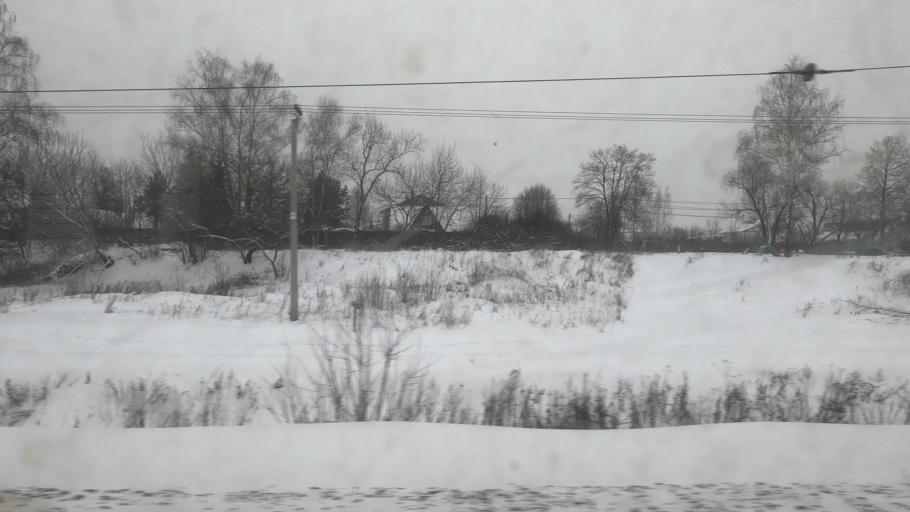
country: RU
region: Moskovskaya
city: Chornaya
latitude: 55.7529
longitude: 38.0457
